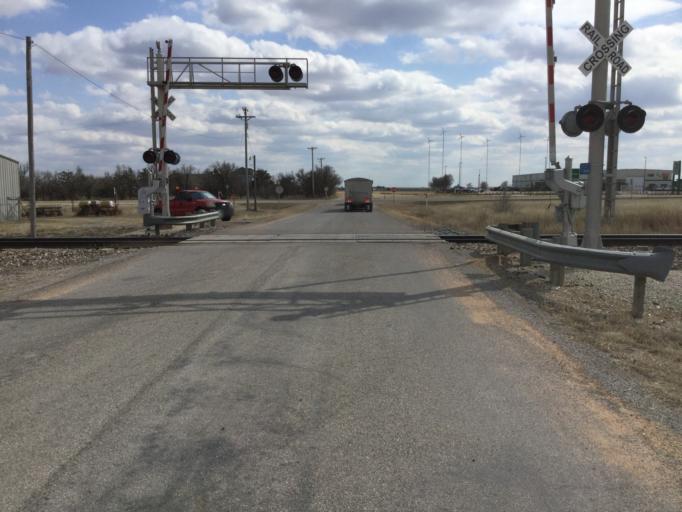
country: US
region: Kansas
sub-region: Kiowa County
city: Greensburg
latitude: 37.6097
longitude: -99.2674
